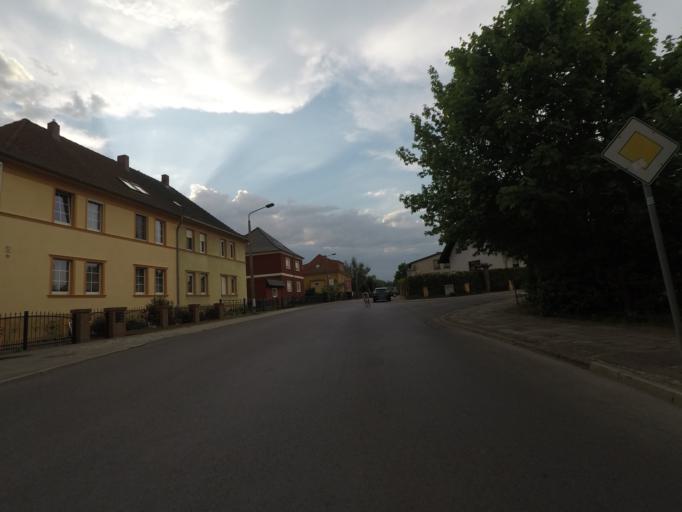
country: DE
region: Brandenburg
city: Melchow
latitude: 52.8437
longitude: 13.7360
